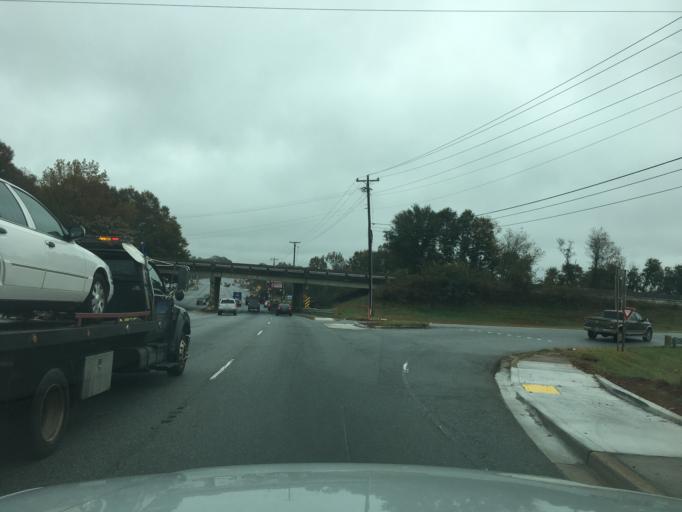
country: US
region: South Carolina
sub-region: Greenville County
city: Gantt
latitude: 34.8022
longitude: -82.4289
